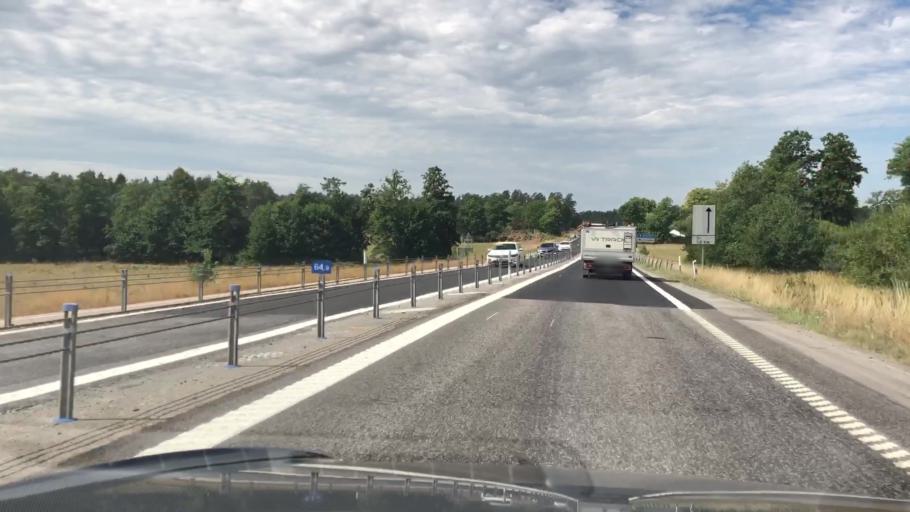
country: SE
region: Blekinge
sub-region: Karlskrona Kommun
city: Nattraby
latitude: 56.1997
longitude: 15.3998
